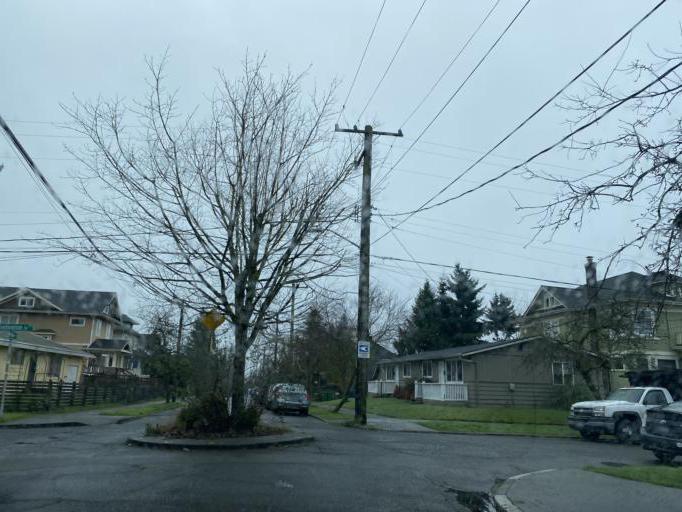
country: US
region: Washington
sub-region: King County
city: Seattle
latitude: 47.6010
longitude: -122.2950
